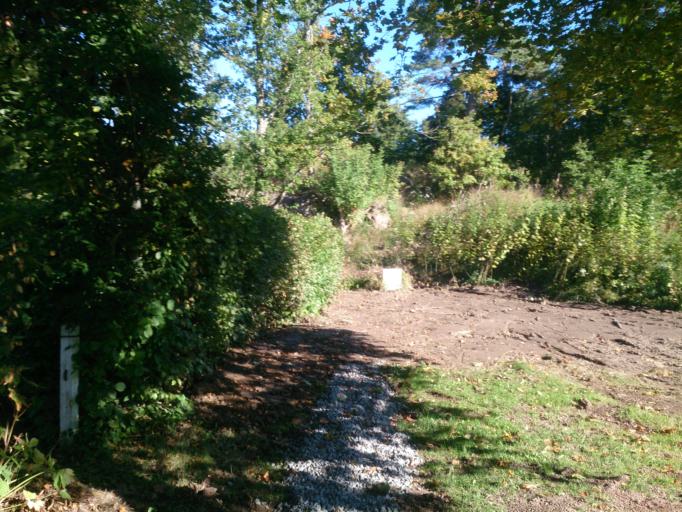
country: SE
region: OEstergoetland
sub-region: Linkopings Kommun
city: Sturefors
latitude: 58.3040
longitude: 15.8723
